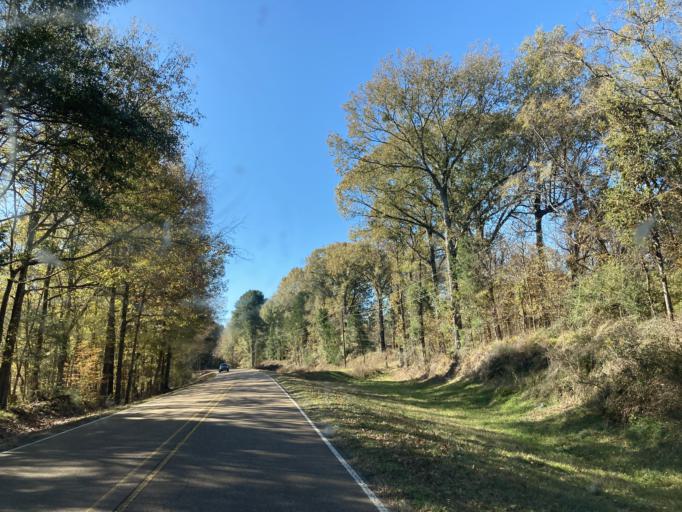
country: US
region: Mississippi
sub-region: Hinds County
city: Lynchburg
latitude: 32.6261
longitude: -90.5213
